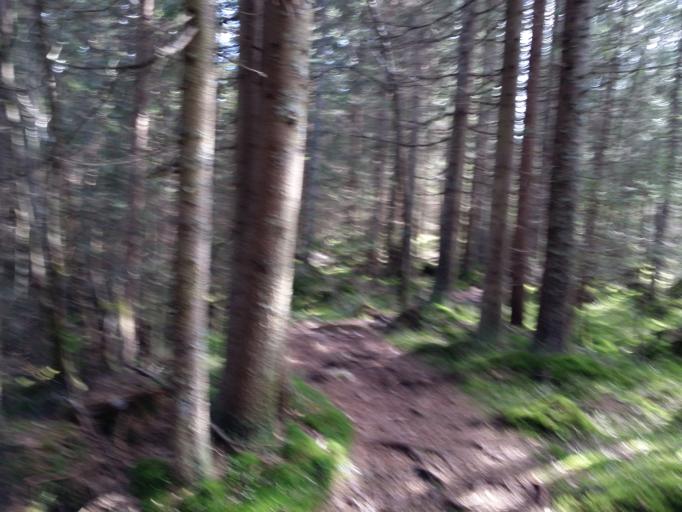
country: NO
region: Oslo
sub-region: Oslo
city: Sjolyststranda
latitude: 59.9904
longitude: 10.7063
